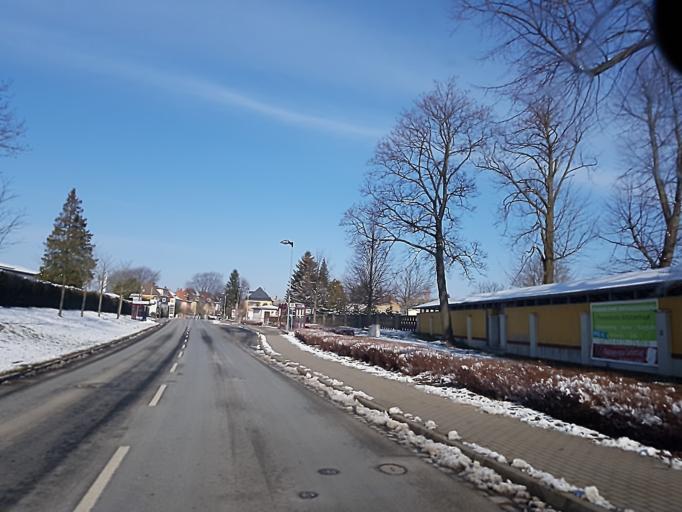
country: DE
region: Saxony
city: Leisnig
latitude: 51.1490
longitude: 12.9283
